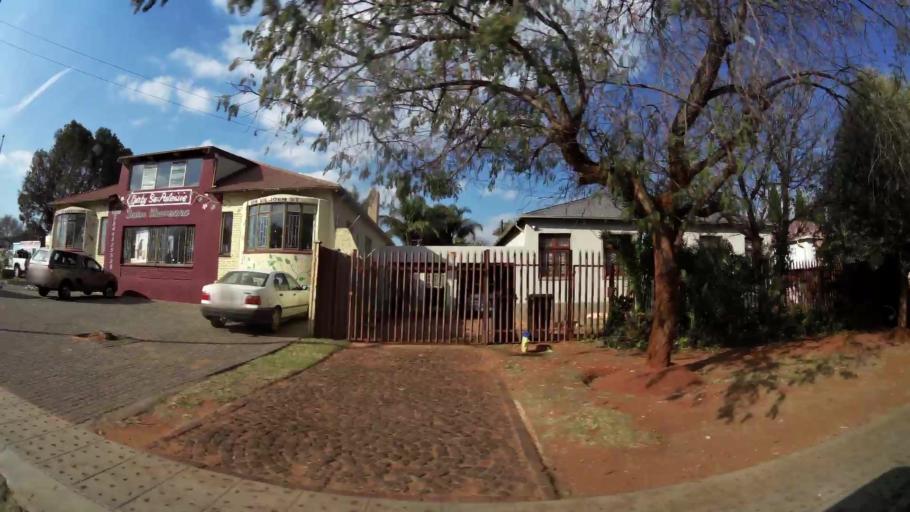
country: ZA
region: Gauteng
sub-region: West Rand District Municipality
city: Krugersdorp
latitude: -26.0884
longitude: 27.7681
